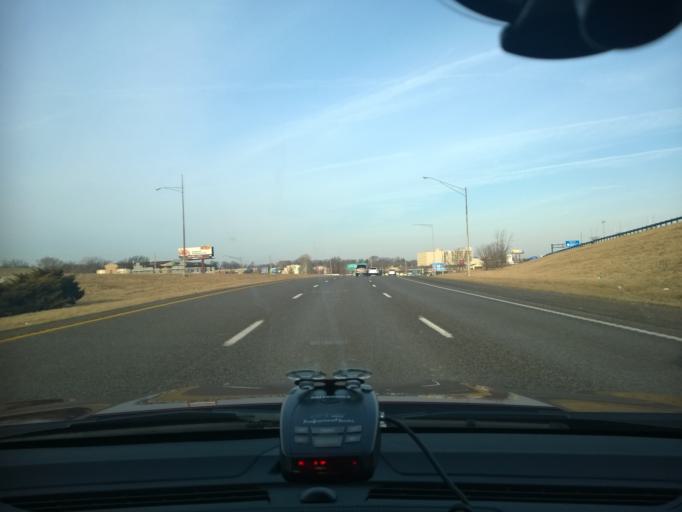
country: US
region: Missouri
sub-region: Saint Louis County
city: Woodson Terrace
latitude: 38.7333
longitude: -90.3502
